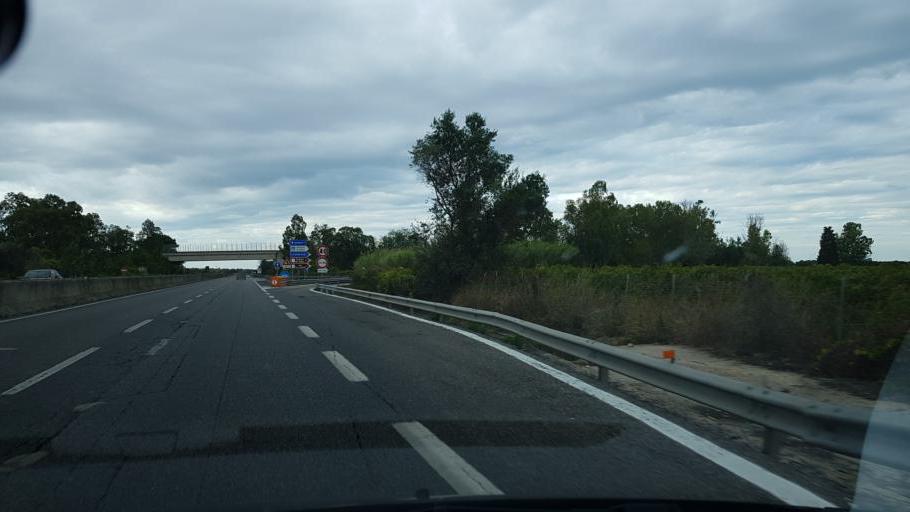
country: IT
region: Apulia
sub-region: Provincia di Brindisi
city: San Pietro Vernotico
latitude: 40.5188
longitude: 18.0188
